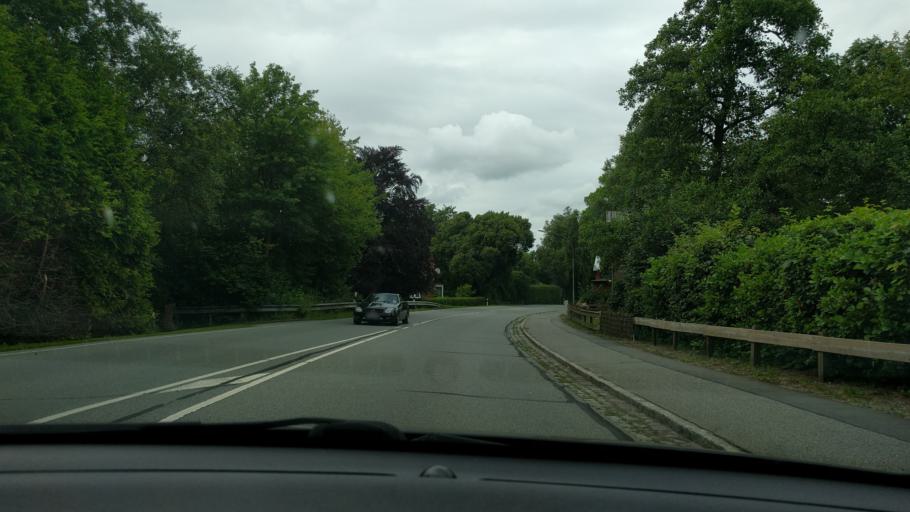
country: DE
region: Schleswig-Holstein
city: Weddingstedt
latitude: 54.2308
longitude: 9.0795
